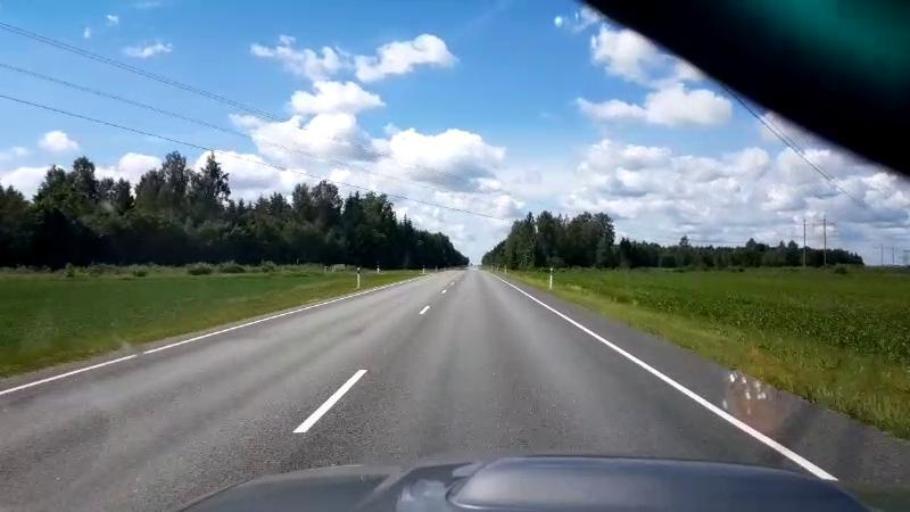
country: EE
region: Laeaene-Virumaa
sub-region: Tapa vald
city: Tapa
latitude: 59.1879
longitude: 25.8059
